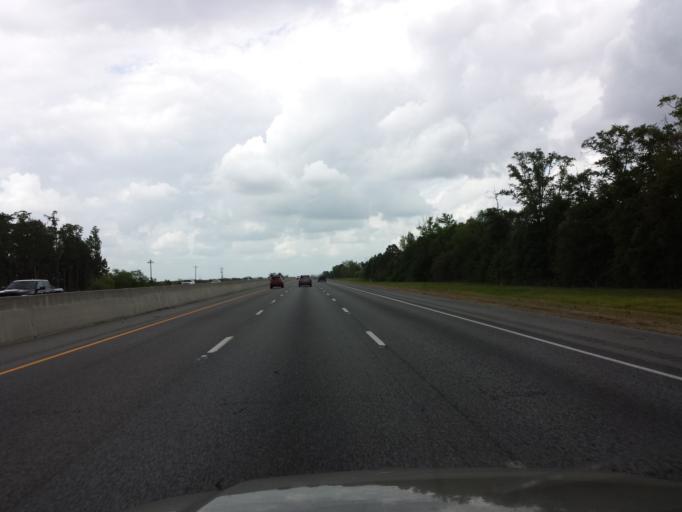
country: US
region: Georgia
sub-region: Lowndes County
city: Hahira
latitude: 30.9524
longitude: -83.3757
